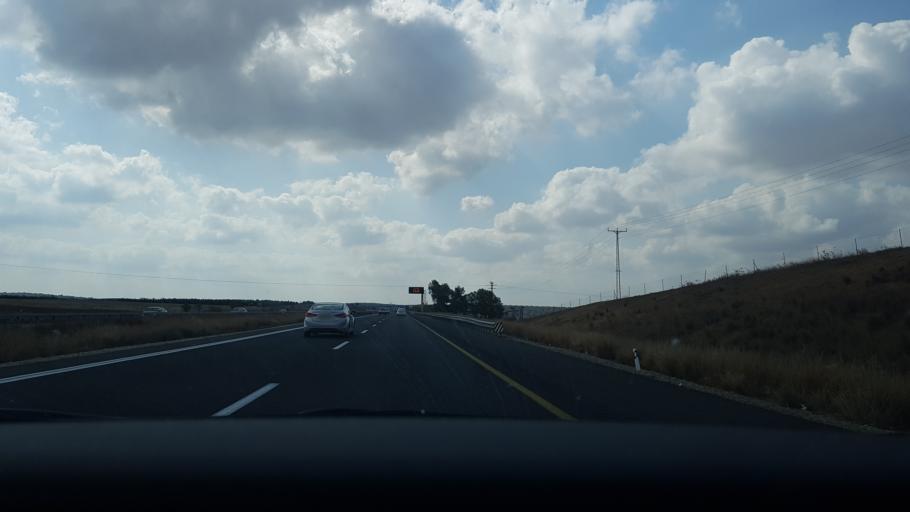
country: IL
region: Southern District
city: Qiryat Gat
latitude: 31.6244
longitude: 34.8148
